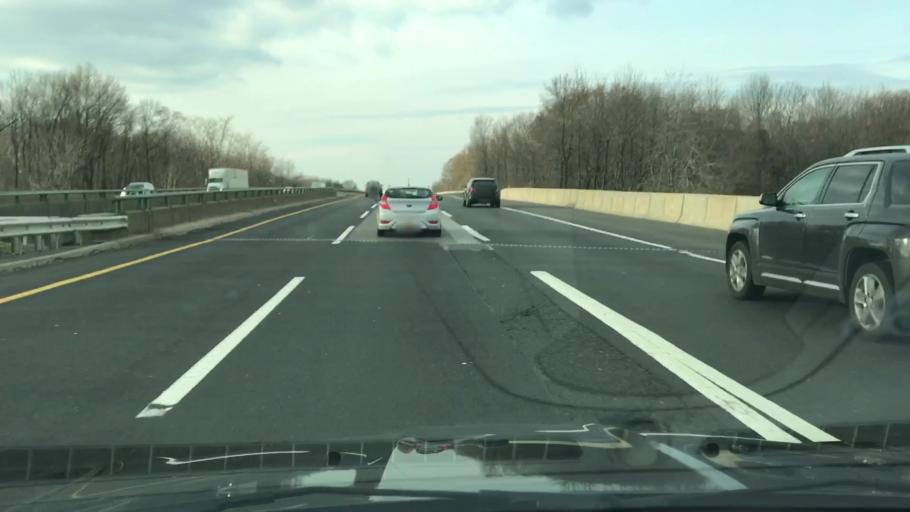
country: US
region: New Jersey
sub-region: Burlington County
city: Roebling
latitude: 40.1026
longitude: -74.7917
